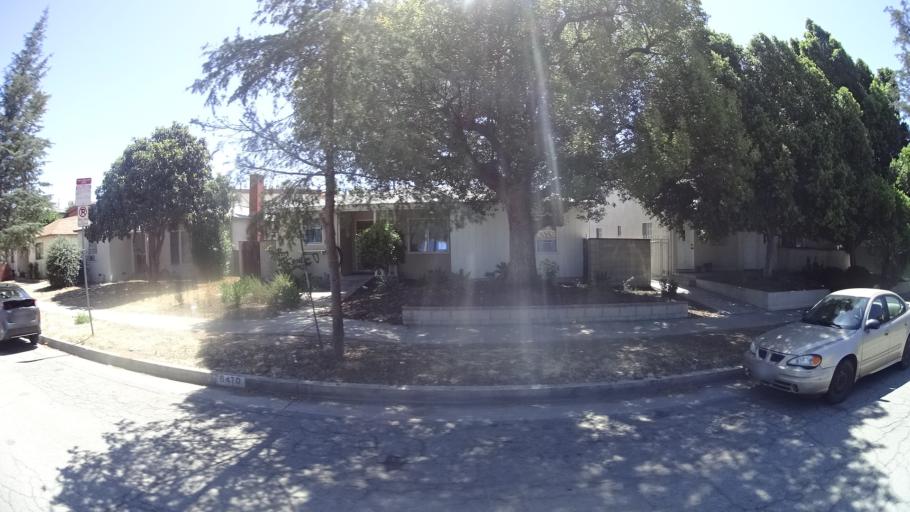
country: US
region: California
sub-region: Los Angeles County
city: Van Nuys
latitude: 34.1886
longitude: -118.5011
